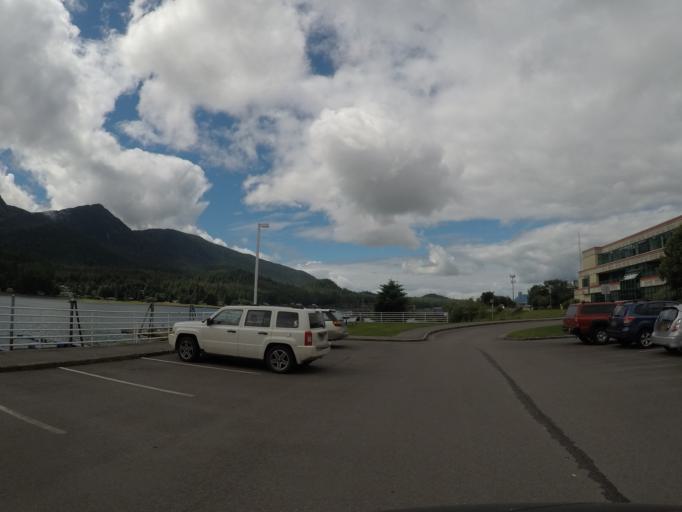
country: US
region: Alaska
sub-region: Juneau City and Borough
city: Juneau
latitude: 58.3266
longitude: -134.4656
